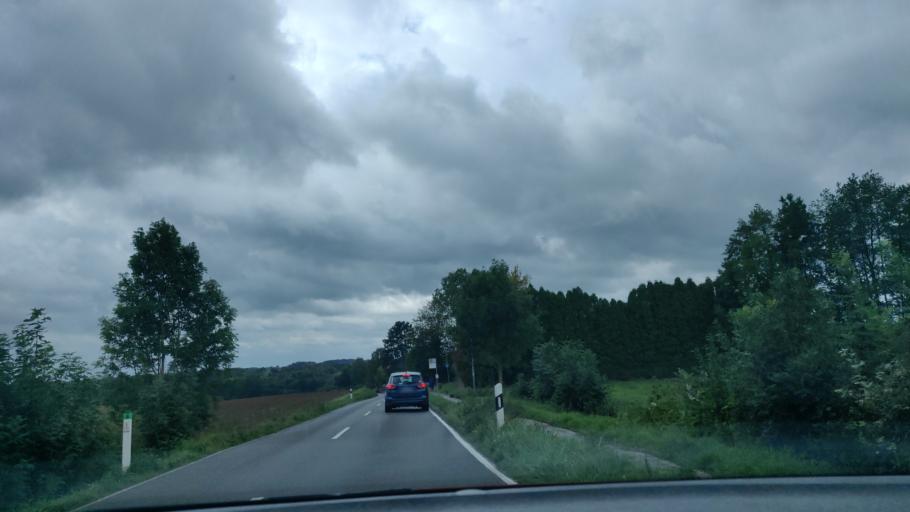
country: DE
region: North Rhine-Westphalia
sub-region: Regierungsbezirk Dusseldorf
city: Heiligenhaus
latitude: 51.2954
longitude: 6.9350
